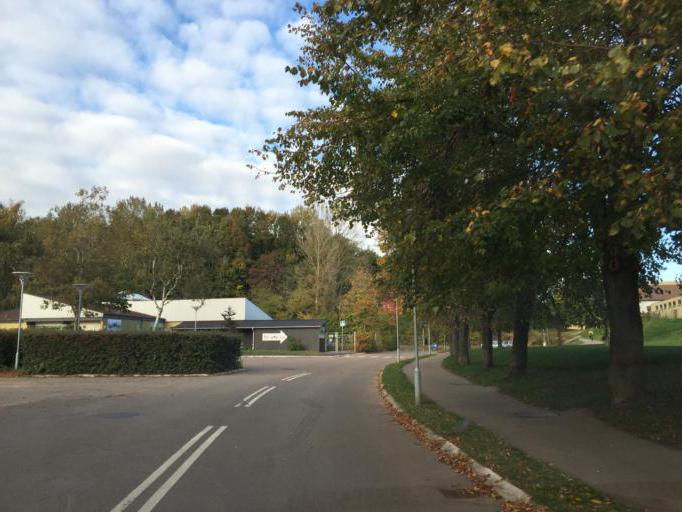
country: DK
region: Zealand
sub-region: Odsherred Kommune
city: Asnaes
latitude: 55.8134
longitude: 11.5001
